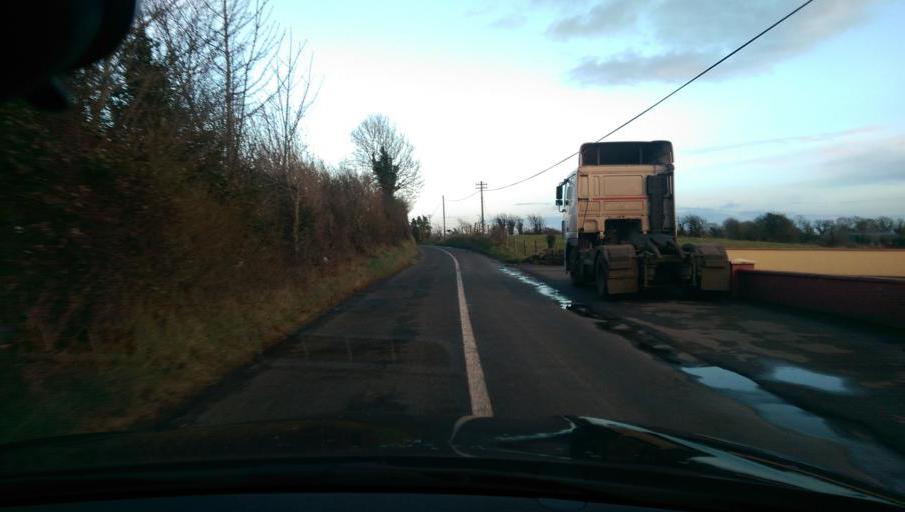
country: IE
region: Connaught
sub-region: County Galway
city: Ballinasloe
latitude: 53.3807
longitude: -8.2893
